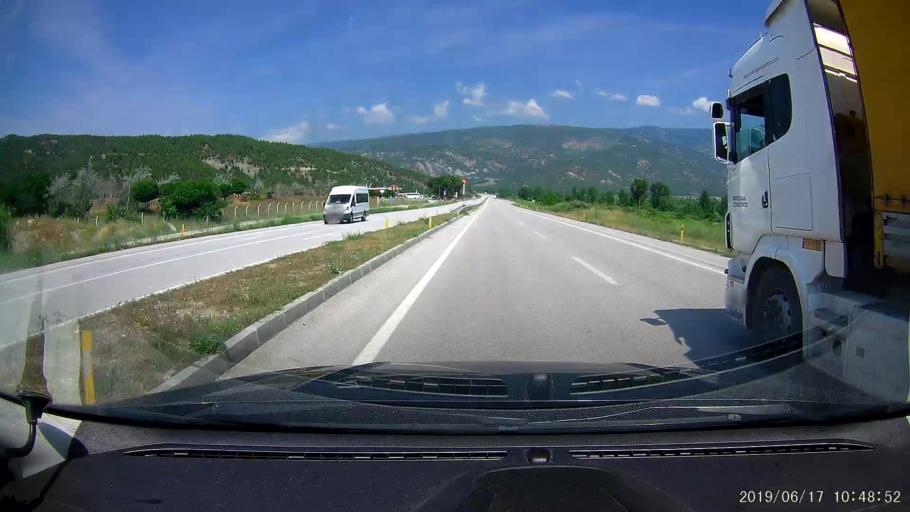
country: TR
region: Corum
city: Hacihamza
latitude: 41.0941
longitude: 34.4219
